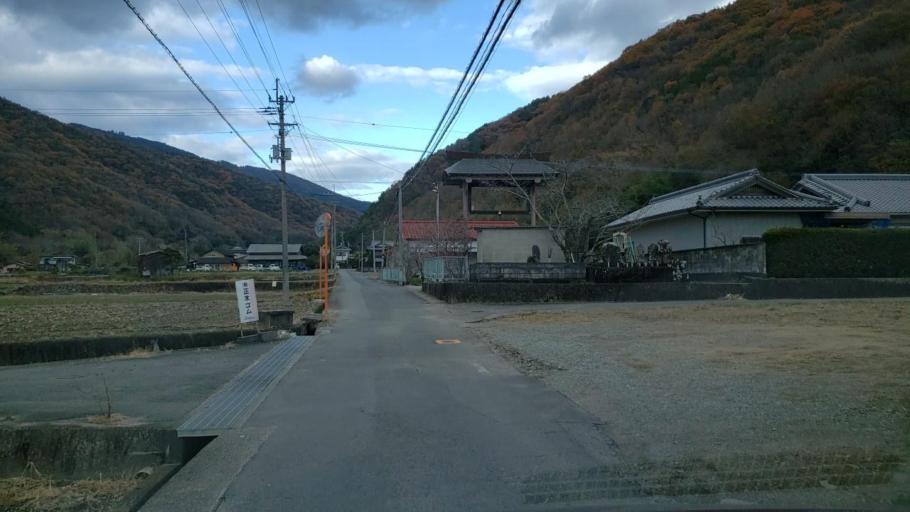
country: JP
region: Tokushima
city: Wakimachi
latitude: 34.1036
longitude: 134.2250
